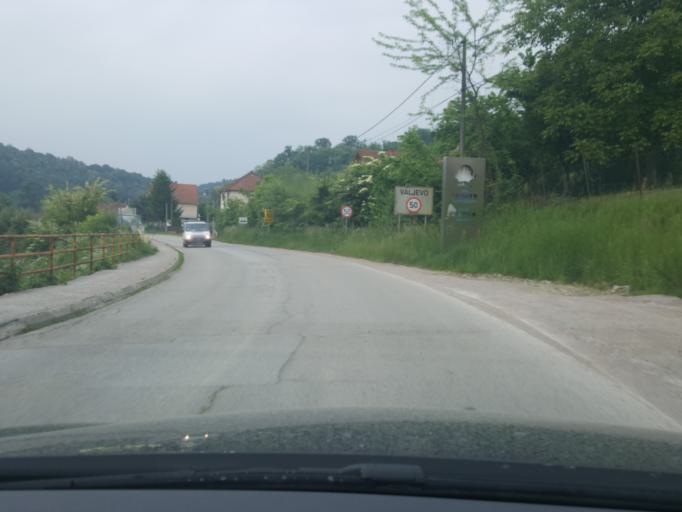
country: RS
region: Central Serbia
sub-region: Kolubarski Okrug
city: Valjevo
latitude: 44.2584
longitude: 19.8653
